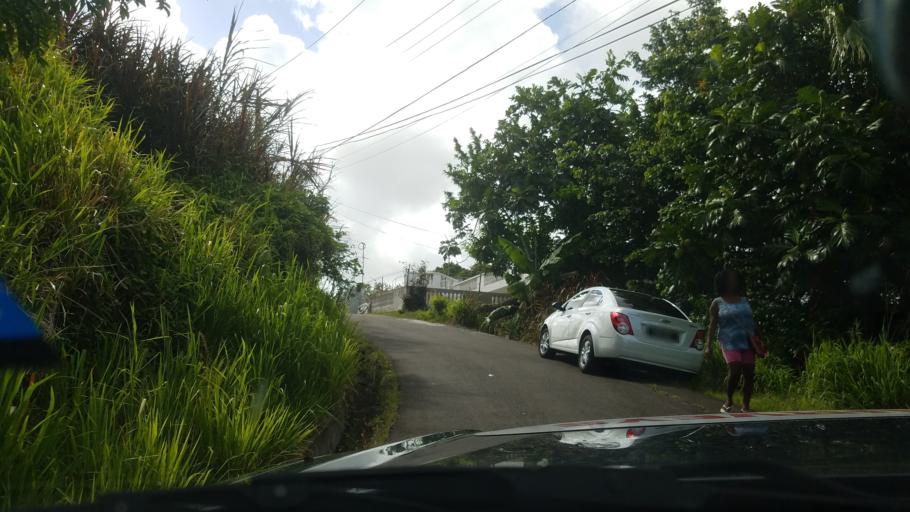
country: LC
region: Castries Quarter
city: Bisee
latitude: 14.0062
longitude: -60.9525
